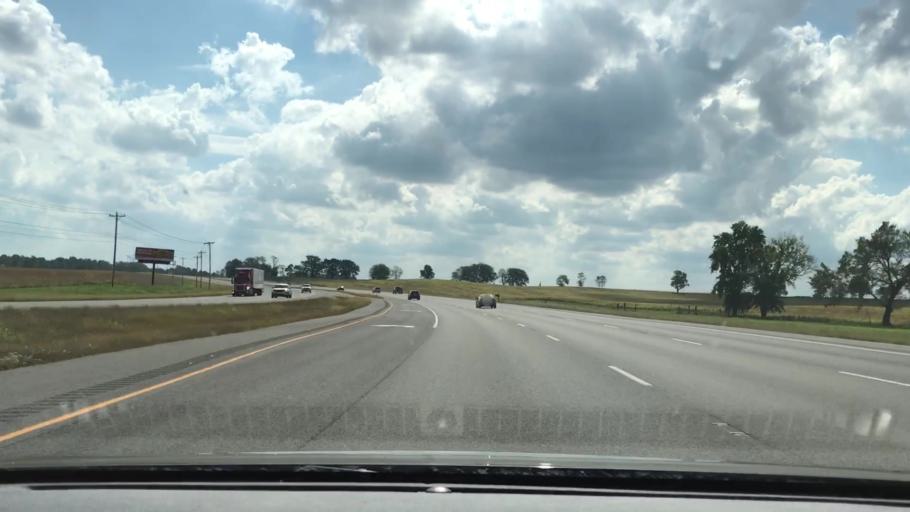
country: US
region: Kentucky
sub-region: Christian County
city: Oak Grove
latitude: 36.6900
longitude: -87.4531
